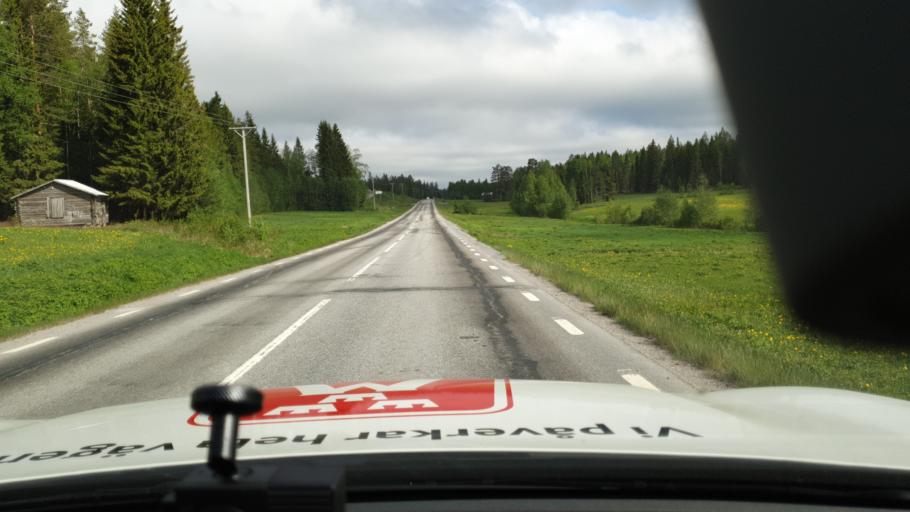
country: SE
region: Vaesterbotten
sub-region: Umea Kommun
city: Roback
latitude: 63.8901
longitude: 20.1983
